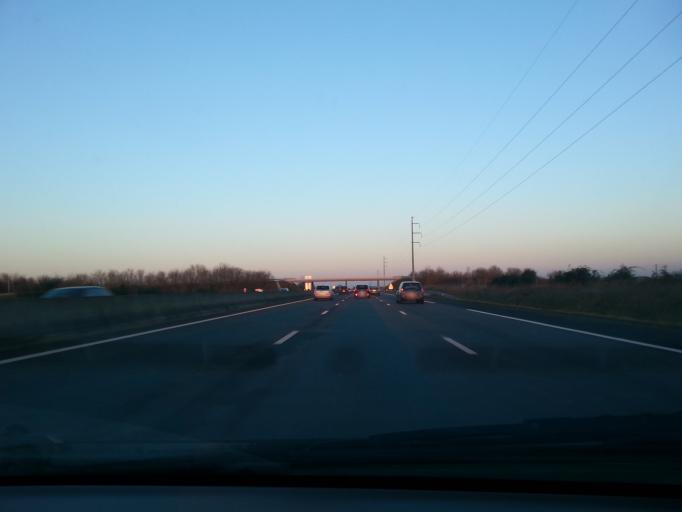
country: FR
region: Centre
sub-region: Departement d'Eure-et-Loir
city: Bailleau-le-Pin
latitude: 48.2985
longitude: 1.2872
